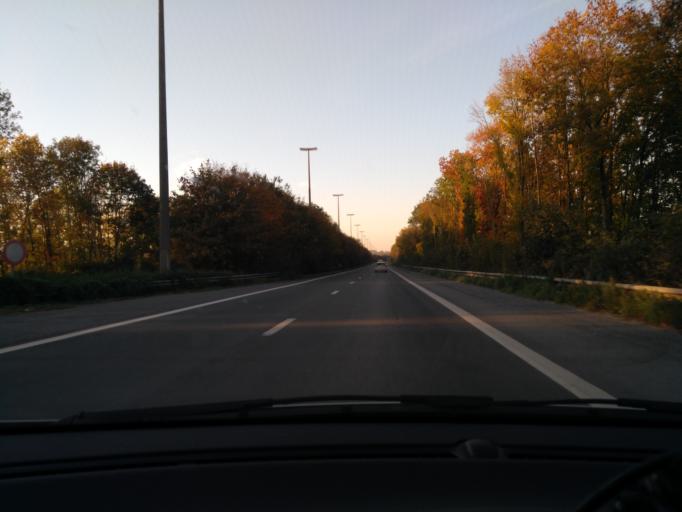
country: BE
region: Wallonia
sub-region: Province du Hainaut
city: Tournai
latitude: 50.6099
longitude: 3.4294
